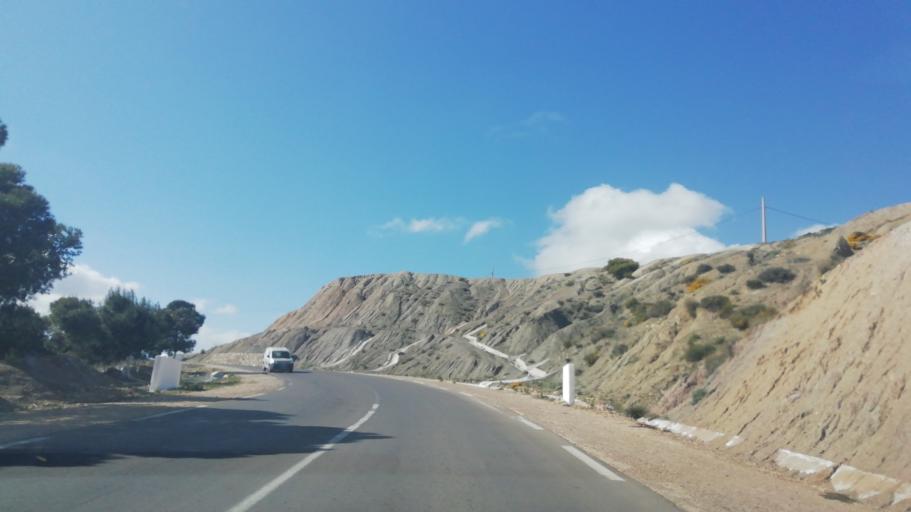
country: DZ
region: Relizane
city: Djidiouia
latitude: 36.0954
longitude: 0.5328
